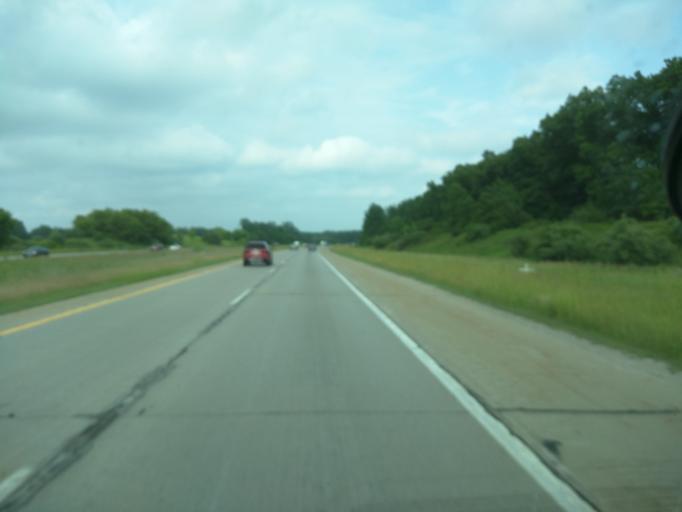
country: US
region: Michigan
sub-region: Clinton County
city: Bath
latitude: 42.8029
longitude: -84.4786
